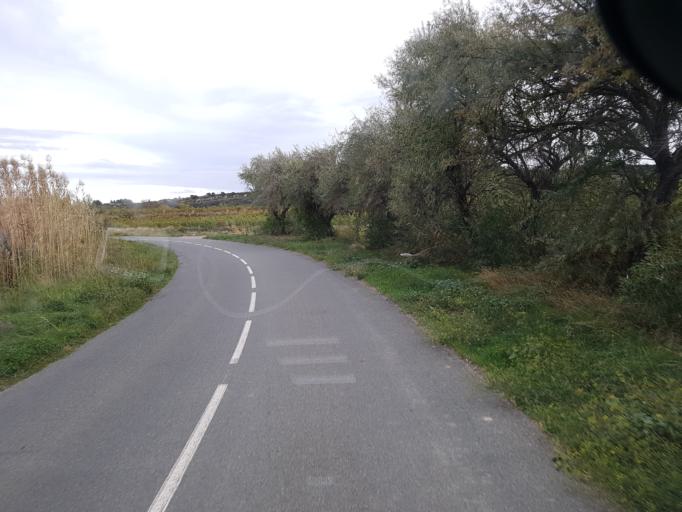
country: FR
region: Languedoc-Roussillon
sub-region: Departement de l'Aude
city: Narbonne
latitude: 43.1388
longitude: 2.9795
